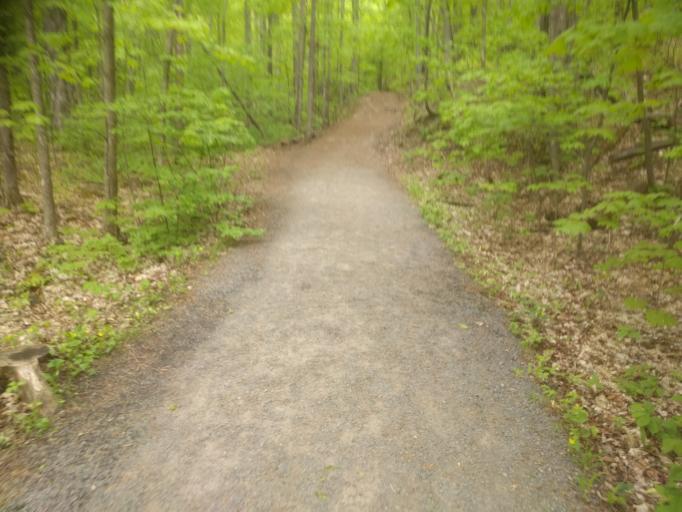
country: CA
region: Quebec
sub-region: Outaouais
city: Wakefield
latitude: 45.5338
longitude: -75.9936
